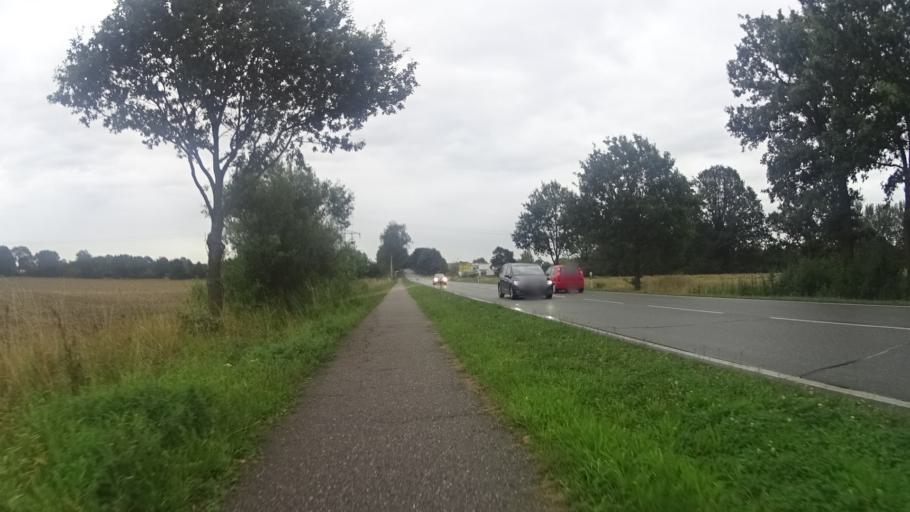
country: DE
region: Schleswig-Holstein
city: Kiebitzreihe
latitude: 53.7804
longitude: 9.6437
